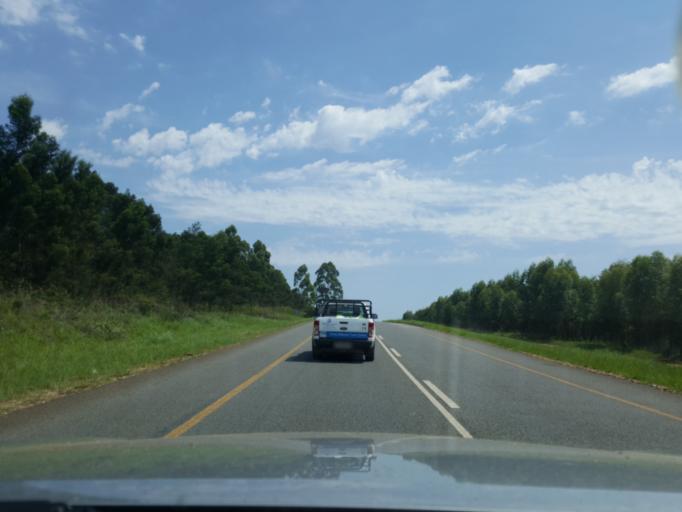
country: ZA
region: Mpumalanga
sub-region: Ehlanzeni District
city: White River
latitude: -25.2636
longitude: 31.0196
